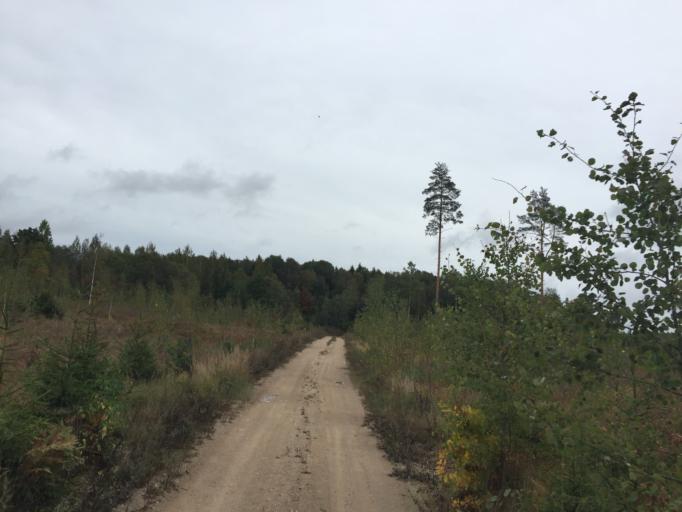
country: LV
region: Malpils
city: Malpils
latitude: 56.9301
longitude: 24.9416
